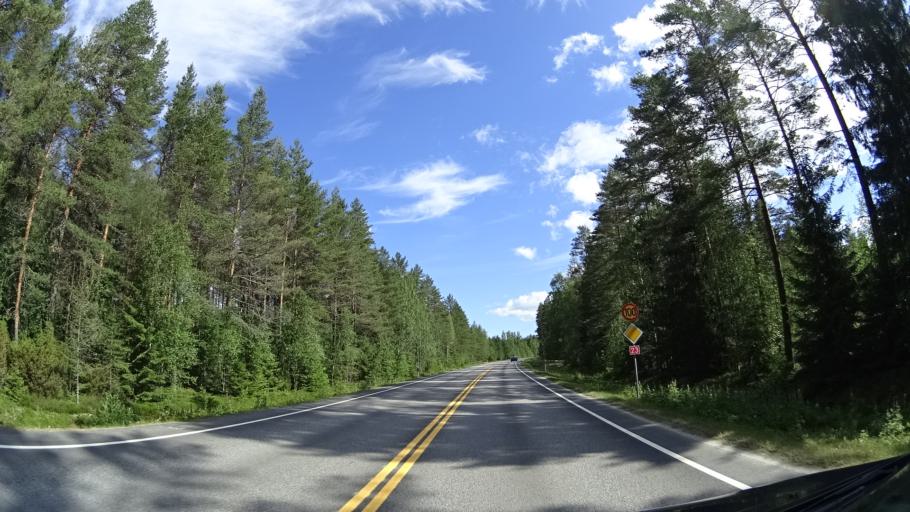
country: FI
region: Pirkanmaa
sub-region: Luoteis-Pirkanmaa
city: Kihnioe
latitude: 62.1237
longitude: 23.1106
